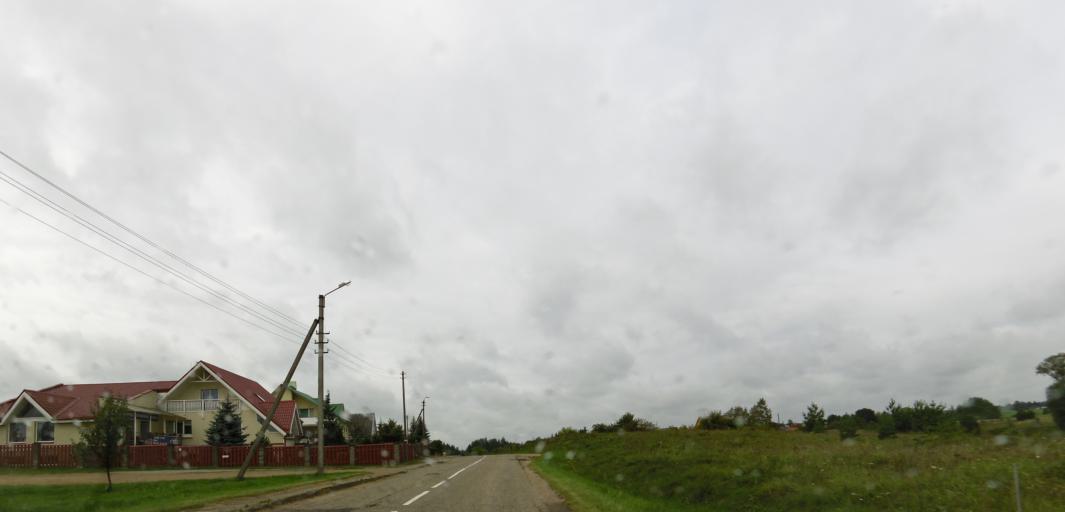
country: LT
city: Moletai
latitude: 55.2303
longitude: 25.4018
